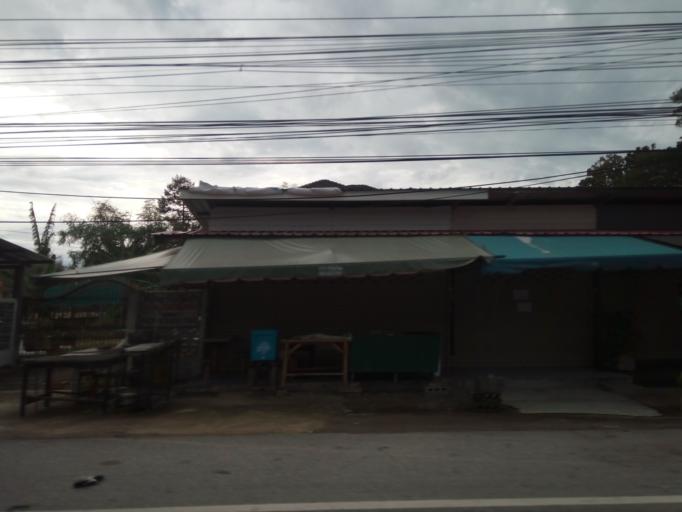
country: TH
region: Phuket
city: Thalang
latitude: 8.0648
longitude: 98.3405
